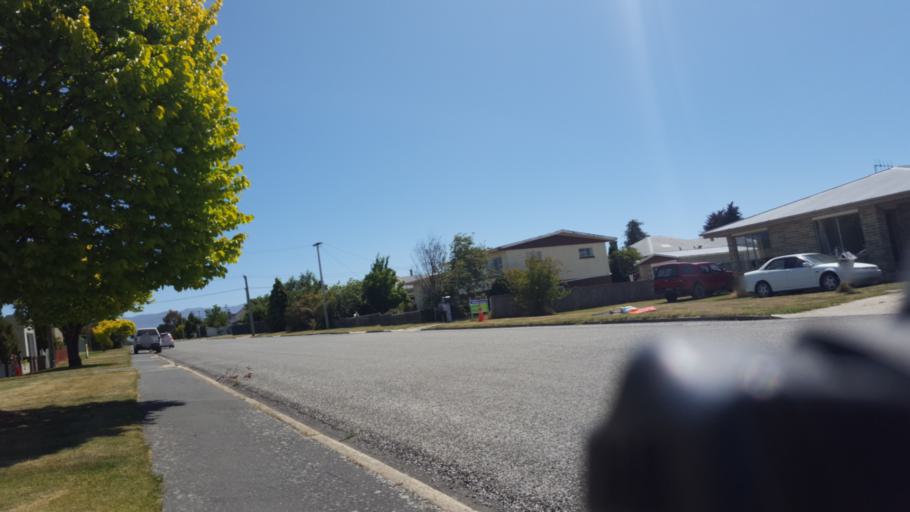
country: NZ
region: Otago
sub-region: Dunedin City
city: Dunedin
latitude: -45.1280
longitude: 170.1060
